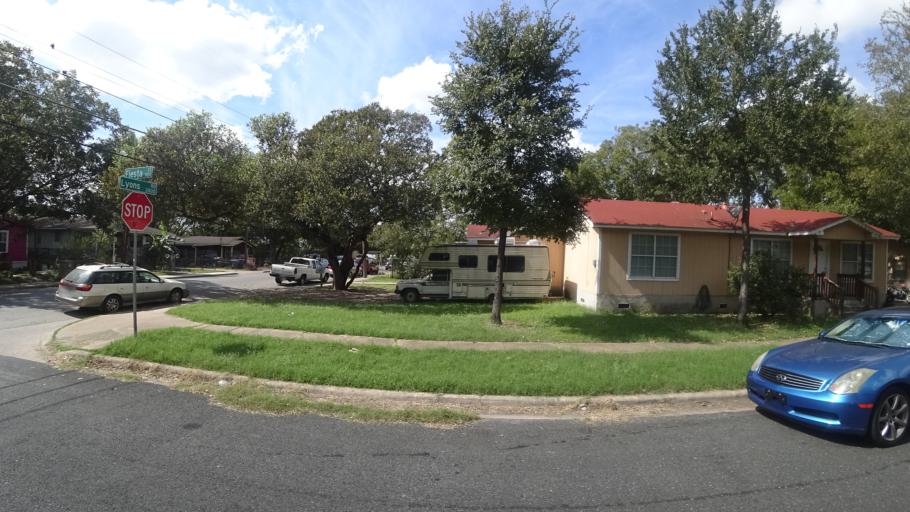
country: US
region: Texas
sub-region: Travis County
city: Austin
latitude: 30.2636
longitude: -97.7066
